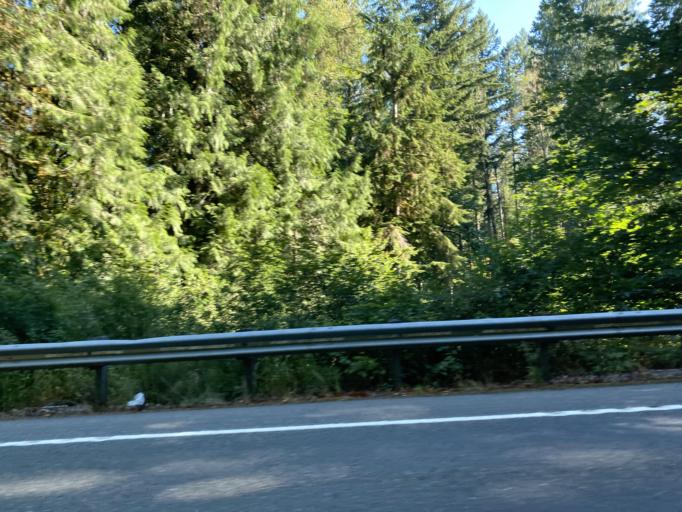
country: US
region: Washington
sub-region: Thurston County
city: Rainier
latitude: 46.9362
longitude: -122.7622
